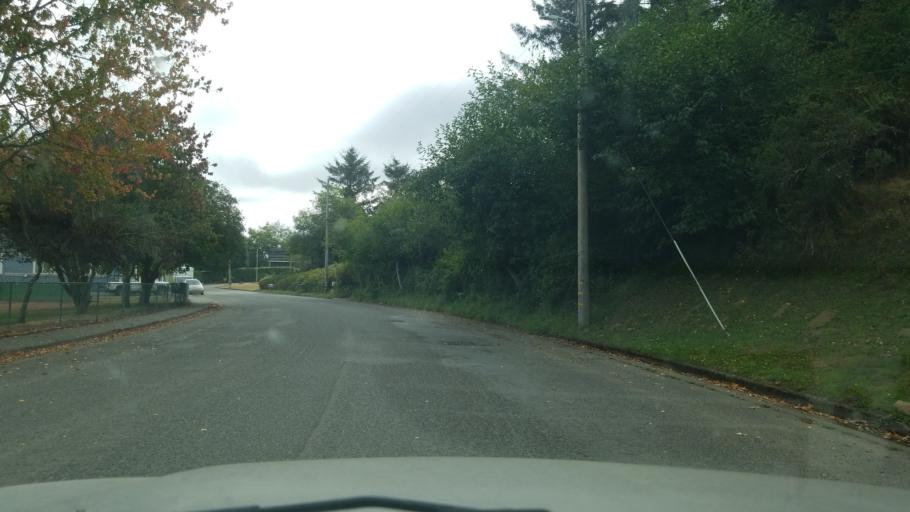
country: US
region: California
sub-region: Humboldt County
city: Ferndale
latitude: 40.5767
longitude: -124.2680
